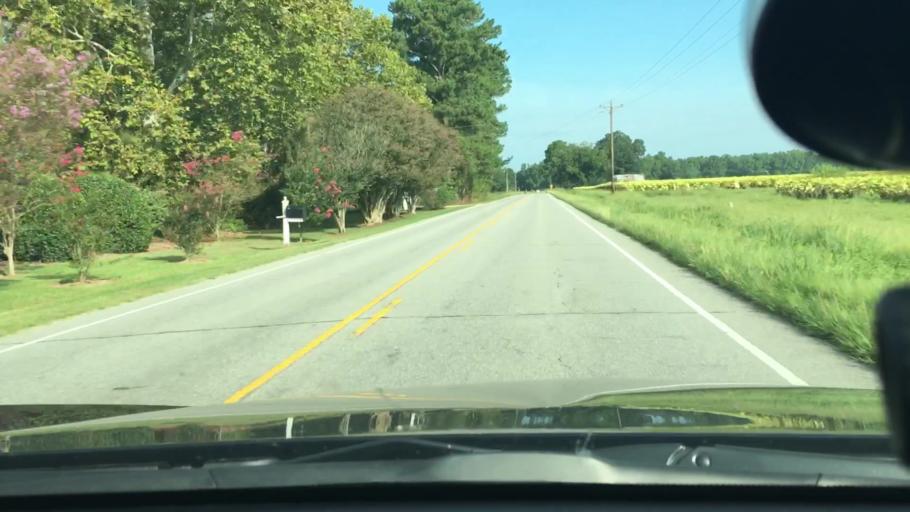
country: US
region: North Carolina
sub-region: Edgecombe County
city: Pinetops
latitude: 35.7492
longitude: -77.5434
